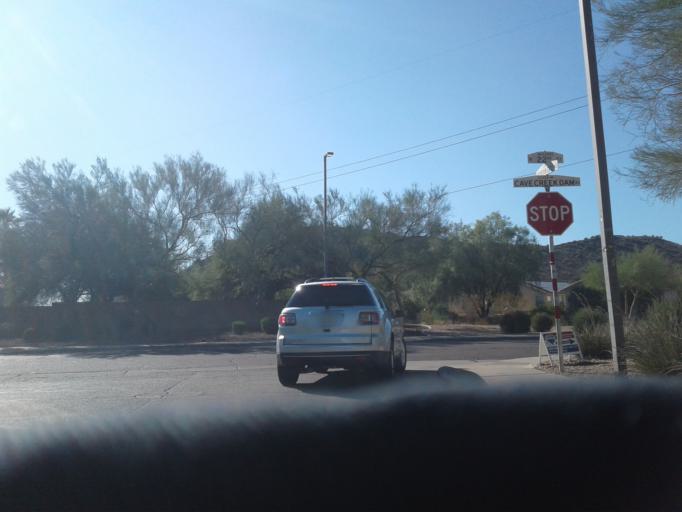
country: US
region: Arizona
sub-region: Maricopa County
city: Cave Creek
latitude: 33.6966
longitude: -112.0352
